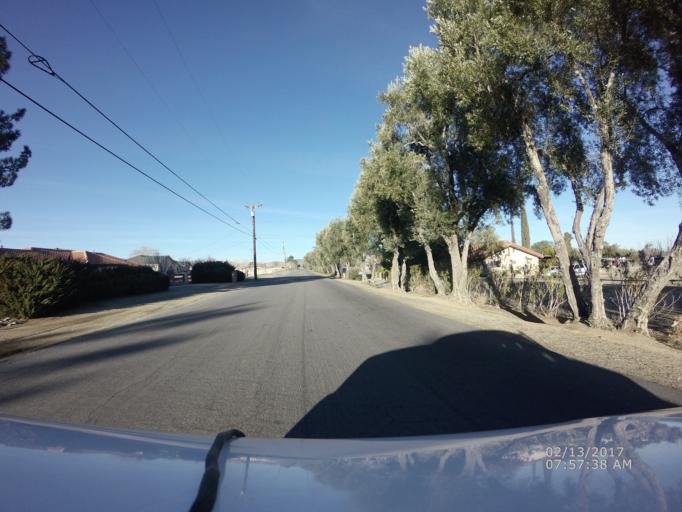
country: US
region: California
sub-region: Los Angeles County
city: Littlerock
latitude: 34.5283
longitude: -117.9865
